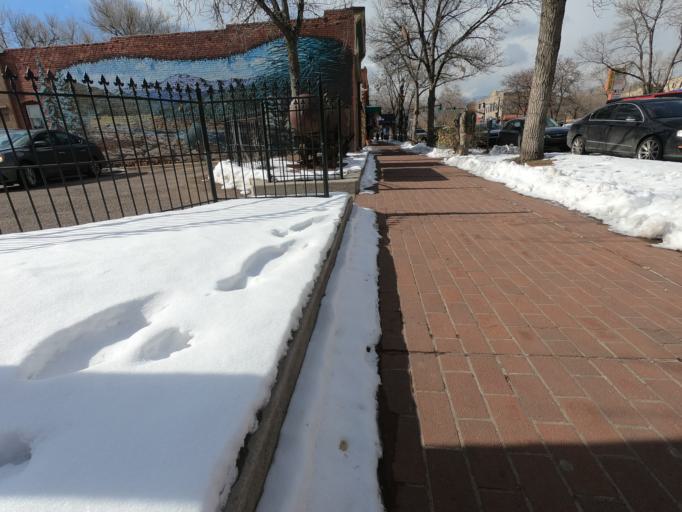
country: US
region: Colorado
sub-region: El Paso County
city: Colorado Springs
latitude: 38.8484
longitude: -104.8650
